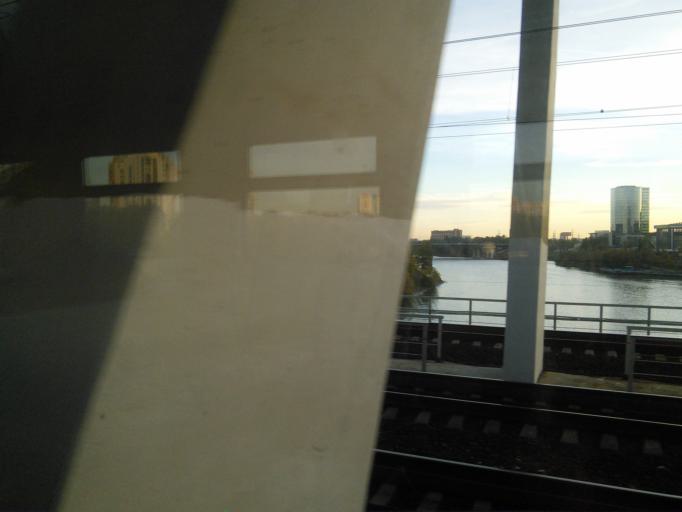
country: RU
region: Moskovskaya
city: Levoberezhnaya
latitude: 55.8895
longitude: 37.4632
